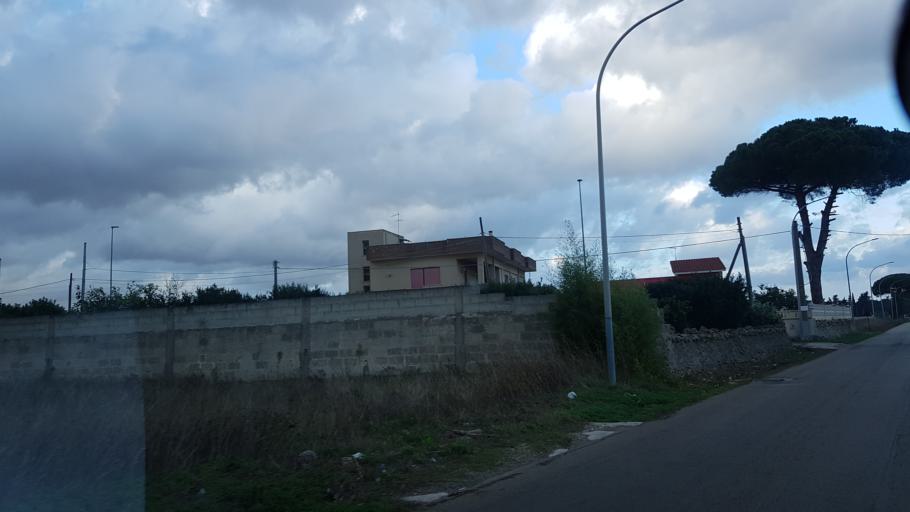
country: IT
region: Apulia
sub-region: Provincia di Brindisi
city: San Pietro Vernotico
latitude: 40.4949
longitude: 18.0018
